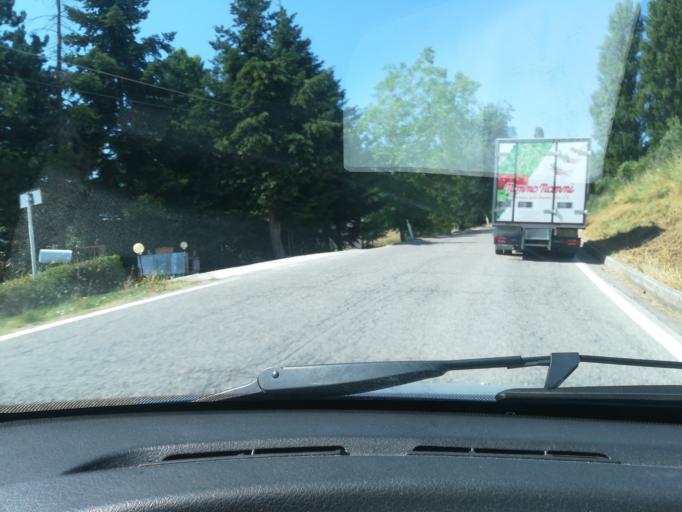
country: IT
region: The Marches
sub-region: Provincia di Macerata
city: San Ginesio
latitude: 43.1082
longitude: 13.3378
